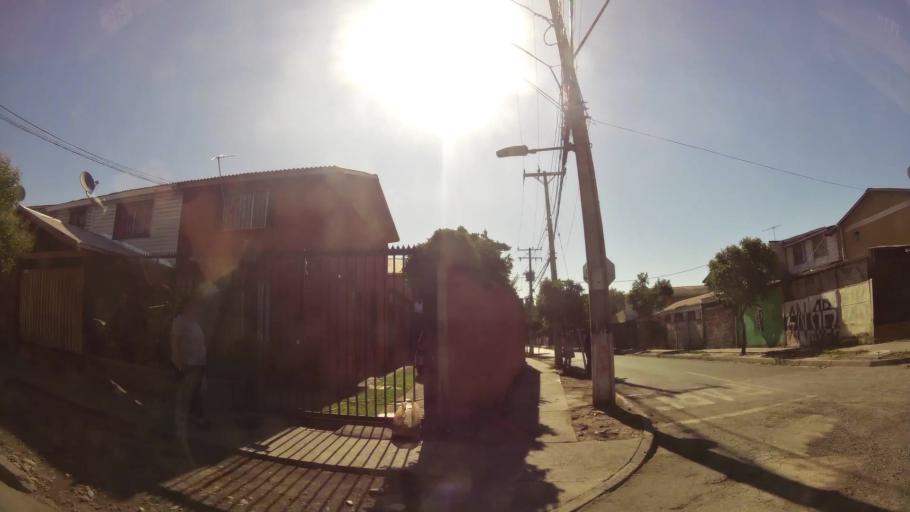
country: CL
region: Santiago Metropolitan
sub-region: Provincia de Maipo
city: San Bernardo
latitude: -33.5904
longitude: -70.6713
